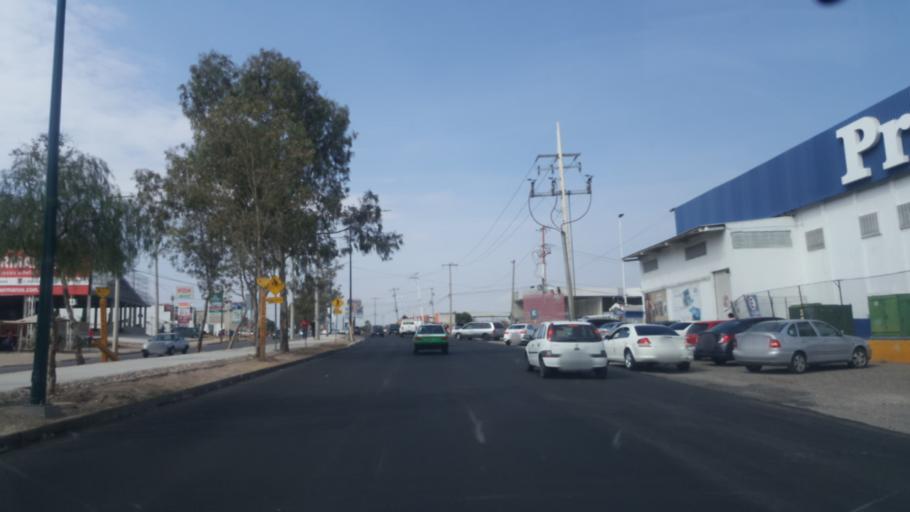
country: MX
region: Guanajuato
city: Leon
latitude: 21.0966
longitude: -101.6325
